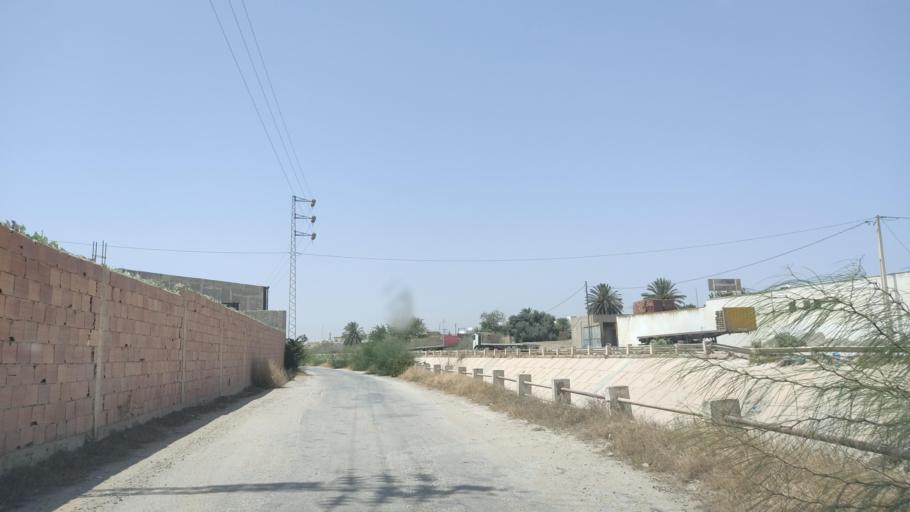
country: TN
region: Safaqis
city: Sfax
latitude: 34.7142
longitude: 10.7315
